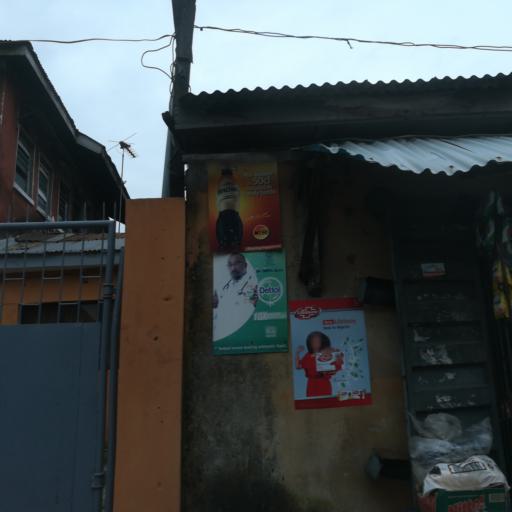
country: NG
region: Lagos
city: Makoko
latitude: 6.5015
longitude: 3.3786
